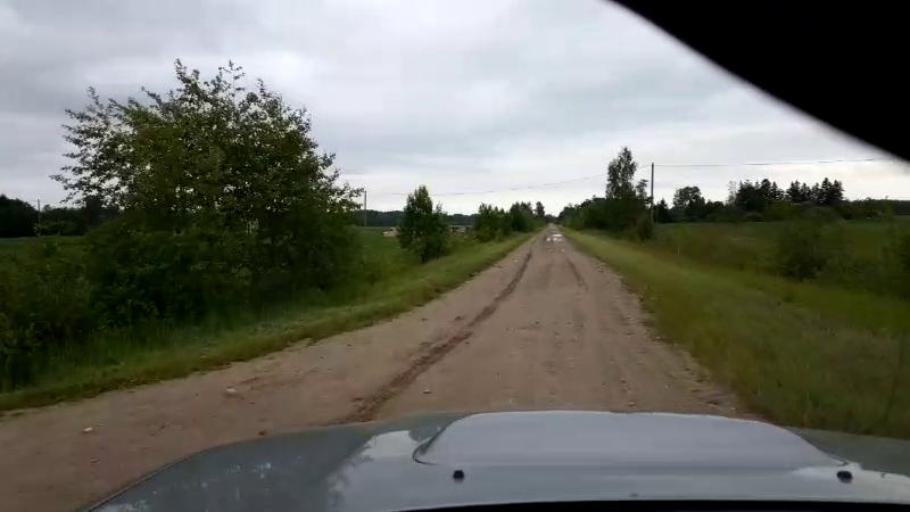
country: EE
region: Paernumaa
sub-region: Halinga vald
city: Parnu-Jaagupi
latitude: 58.5610
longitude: 24.5766
